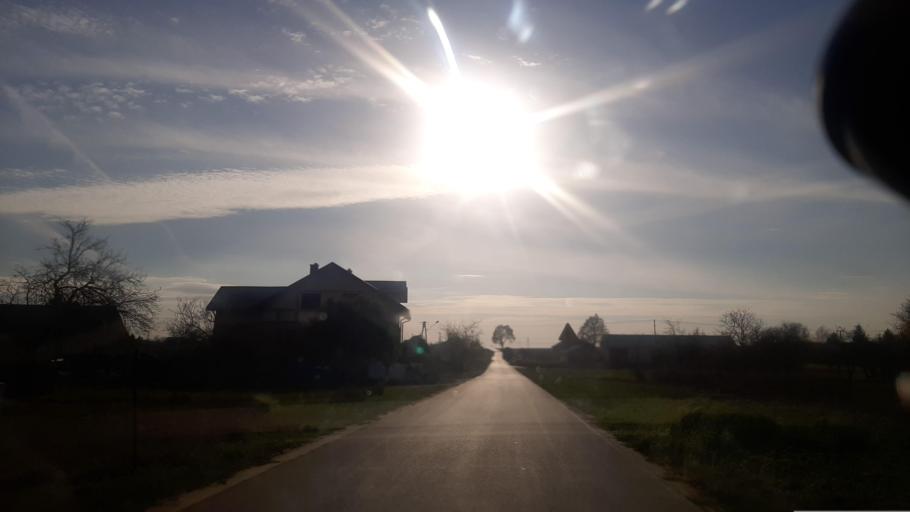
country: PL
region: Lublin Voivodeship
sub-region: Powiat lubelski
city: Garbow
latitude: 51.3886
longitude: 22.3438
